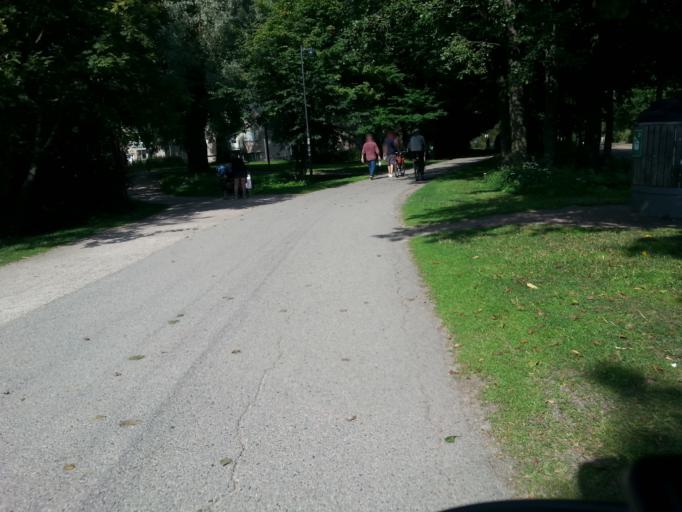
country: FI
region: Uusimaa
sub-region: Helsinki
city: Helsinki
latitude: 60.2150
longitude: 24.9858
